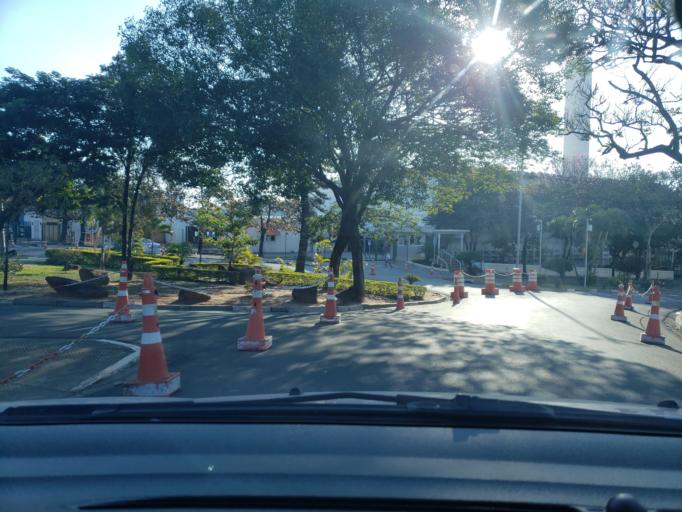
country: BR
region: Sao Paulo
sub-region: Campinas
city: Campinas
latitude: -22.9221
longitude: -47.1193
